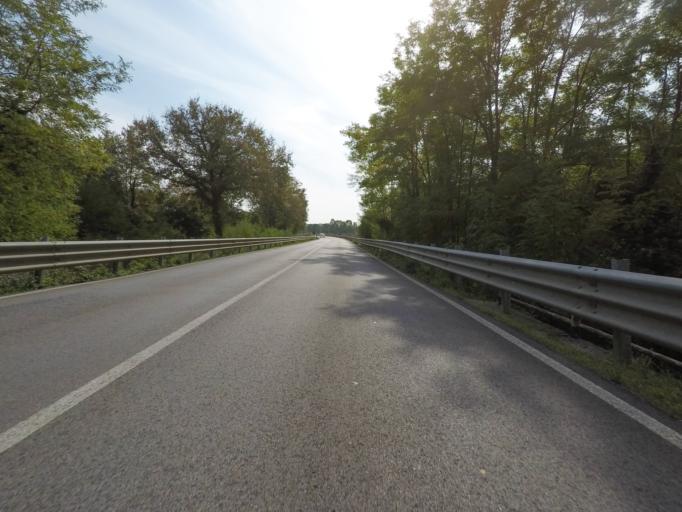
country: IT
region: Tuscany
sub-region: Provincia di Siena
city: Rosia
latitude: 43.1734
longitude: 11.2801
